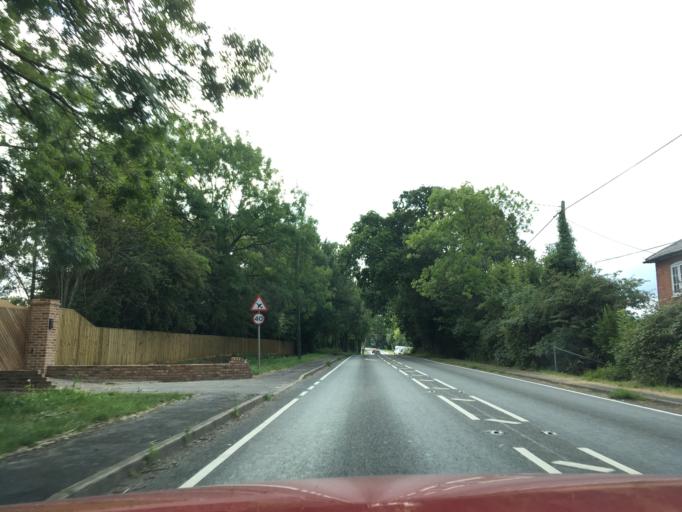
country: GB
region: England
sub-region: Hampshire
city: Bishops Waltham
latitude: 50.9716
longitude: -1.2540
